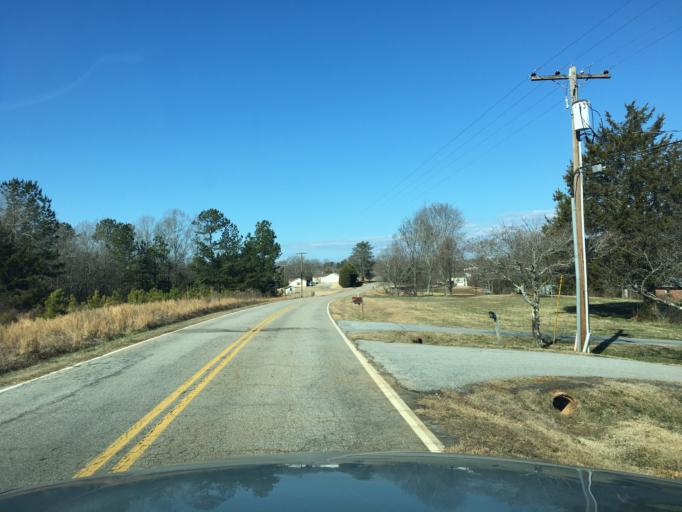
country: US
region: South Carolina
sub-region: Pickens County
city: Pickens
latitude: 34.8558
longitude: -82.7733
